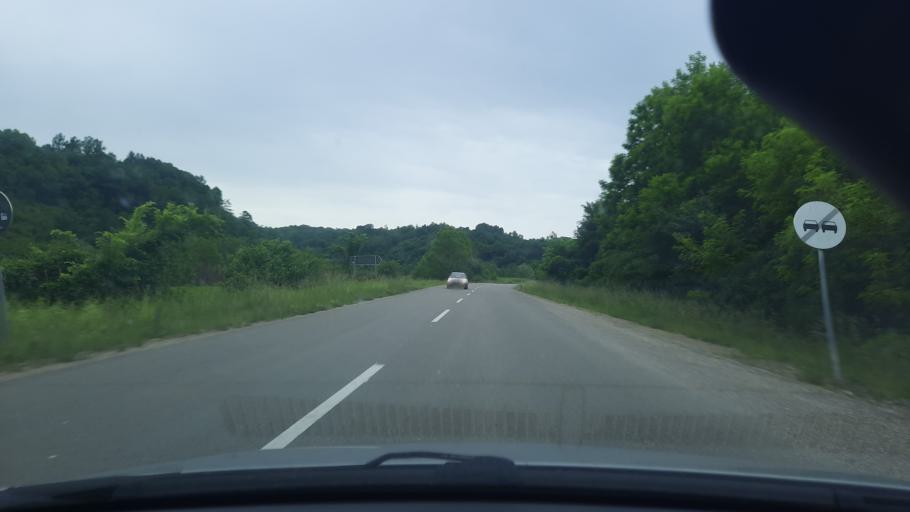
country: RS
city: Bukor
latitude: 44.5190
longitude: 19.5122
